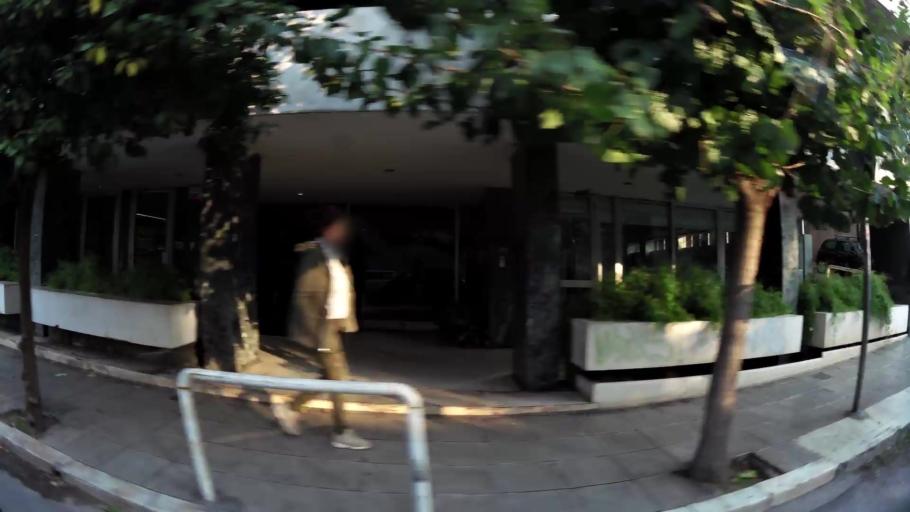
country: GR
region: Attica
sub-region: Nomarchia Athinas
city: Vyronas
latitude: 37.9794
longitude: 23.7469
